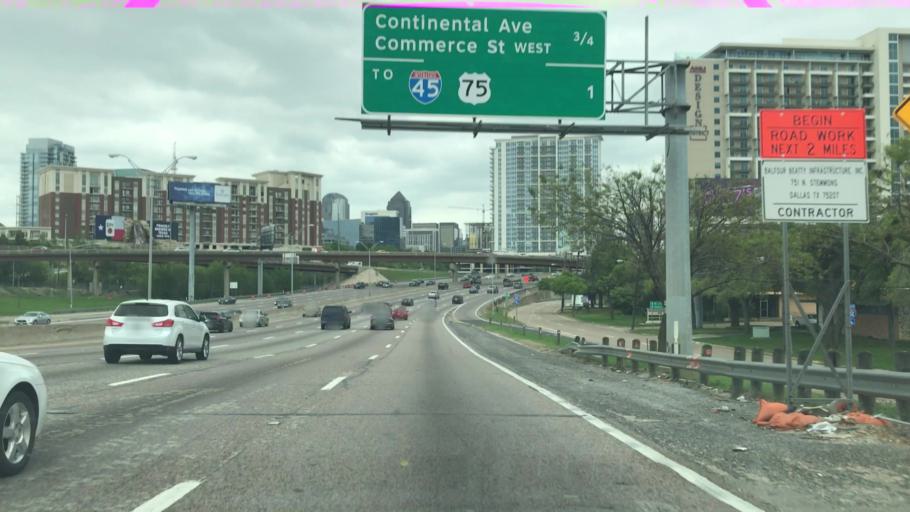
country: US
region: Texas
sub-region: Dallas County
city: Dallas
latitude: 32.7978
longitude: -96.8179
